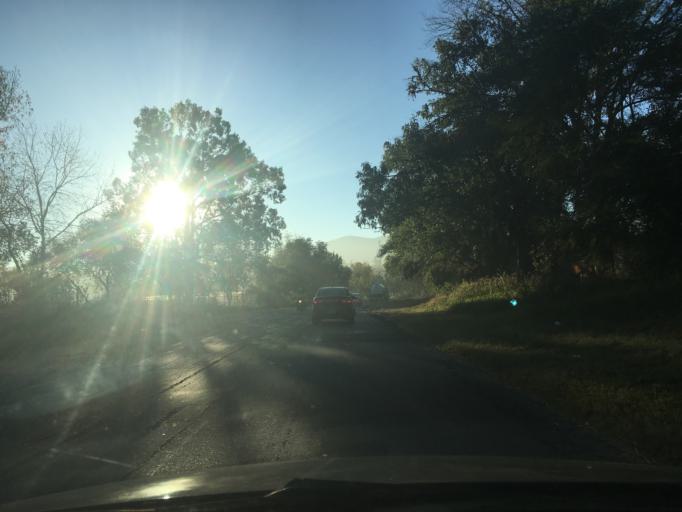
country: MX
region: Michoacan
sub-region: Morelia
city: Morelos
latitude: 19.6613
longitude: -101.2297
